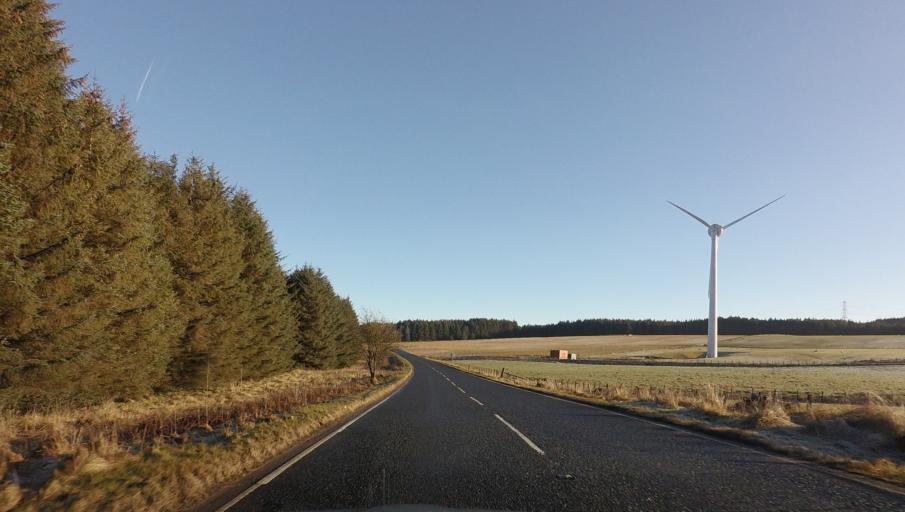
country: GB
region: Scotland
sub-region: West Lothian
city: Fauldhouse
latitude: 55.8107
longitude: -3.7197
